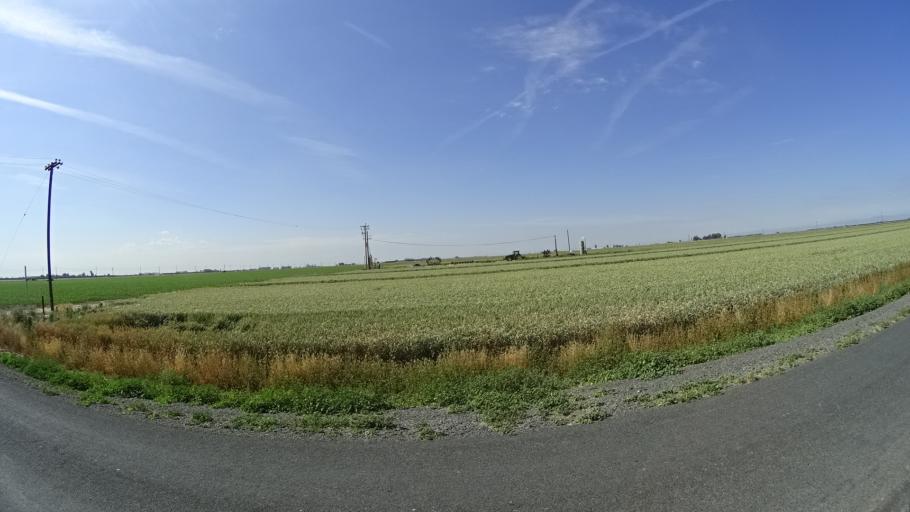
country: US
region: California
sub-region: Kings County
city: Home Garden
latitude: 36.2548
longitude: -119.6597
